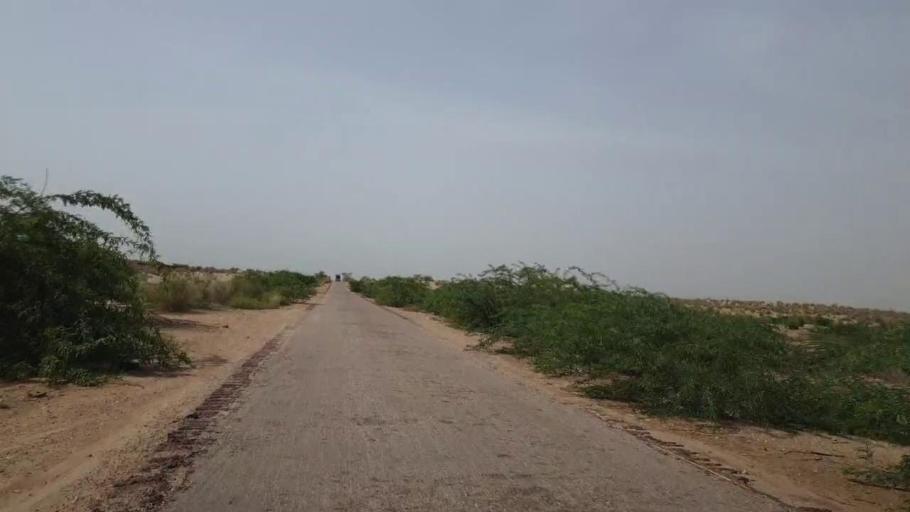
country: PK
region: Sindh
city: Bandhi
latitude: 26.5545
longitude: 68.3832
